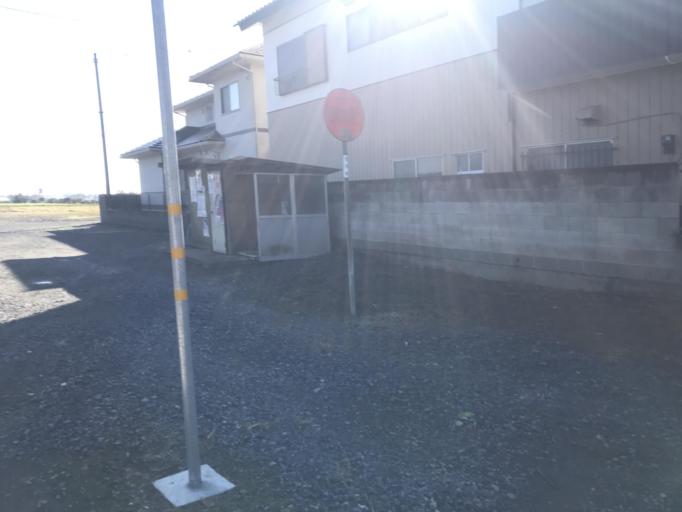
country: JP
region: Ibaraki
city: Sakai
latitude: 36.1811
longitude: 139.8099
